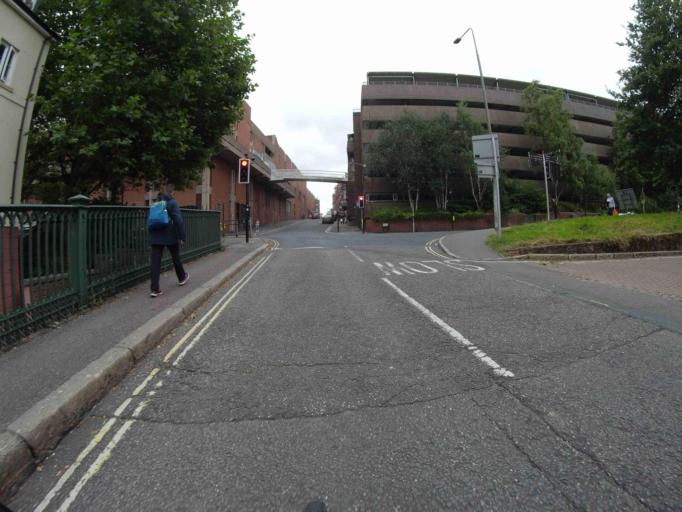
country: GB
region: England
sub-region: Devon
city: Exeter
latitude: 50.7237
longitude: -3.5347
